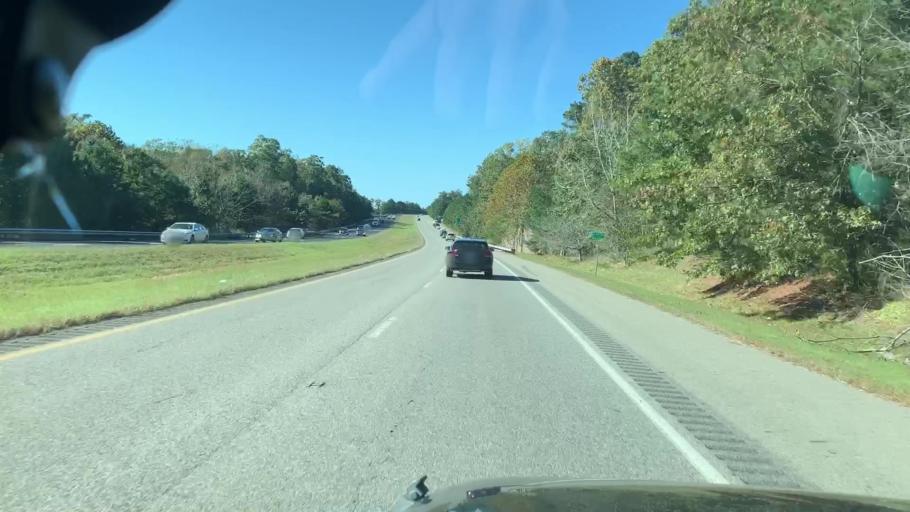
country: US
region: Virginia
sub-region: James City County
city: Williamsburg
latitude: 37.2680
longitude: -76.7453
